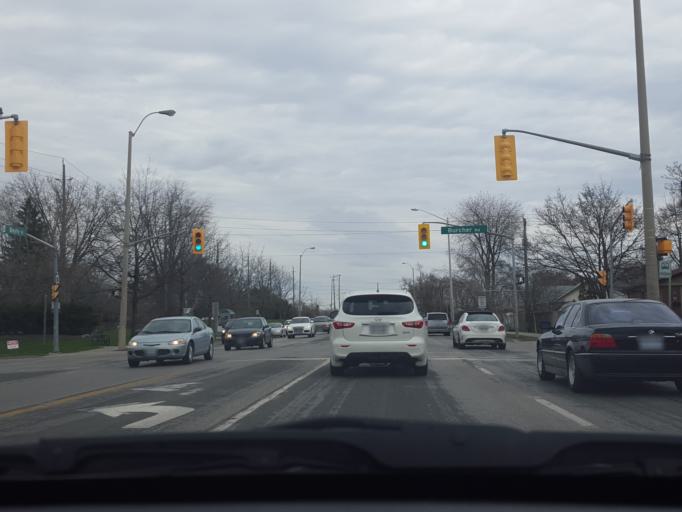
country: CA
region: Ontario
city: Ajax
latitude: 43.8452
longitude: -79.0126
